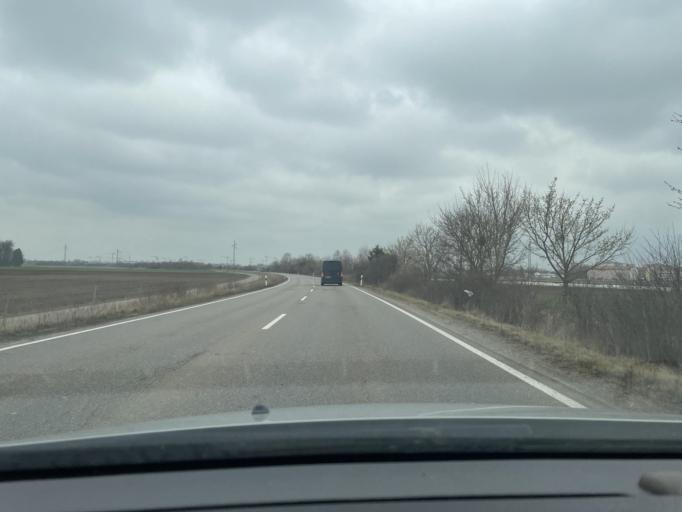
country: DE
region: Bavaria
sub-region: Upper Bavaria
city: Germering
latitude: 48.1427
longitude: 11.3768
